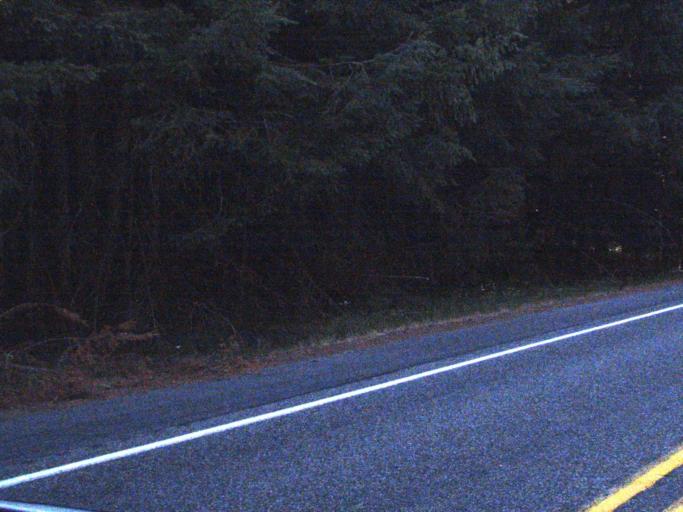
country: US
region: Washington
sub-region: King County
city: Riverbend
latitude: 47.1042
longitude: -121.5925
